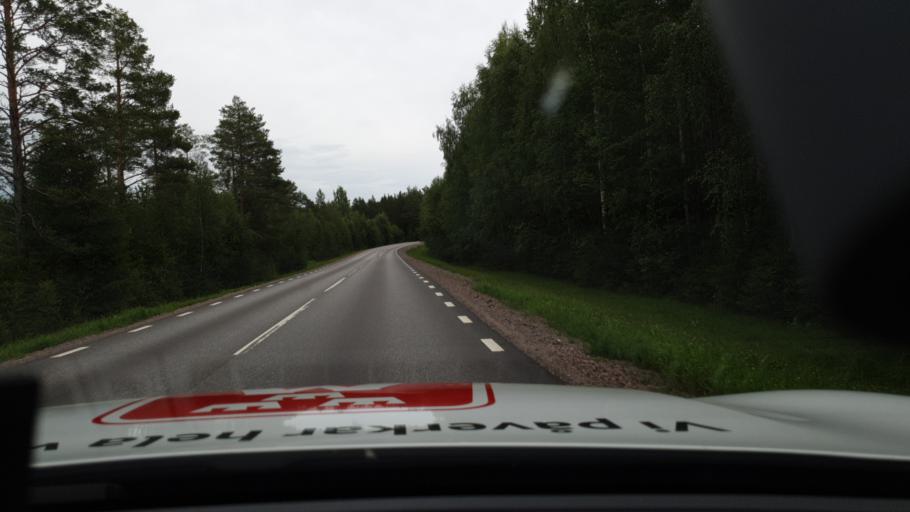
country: SE
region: Norrbotten
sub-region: Lulea Kommun
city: Gammelstad
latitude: 65.5249
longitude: 21.9719
